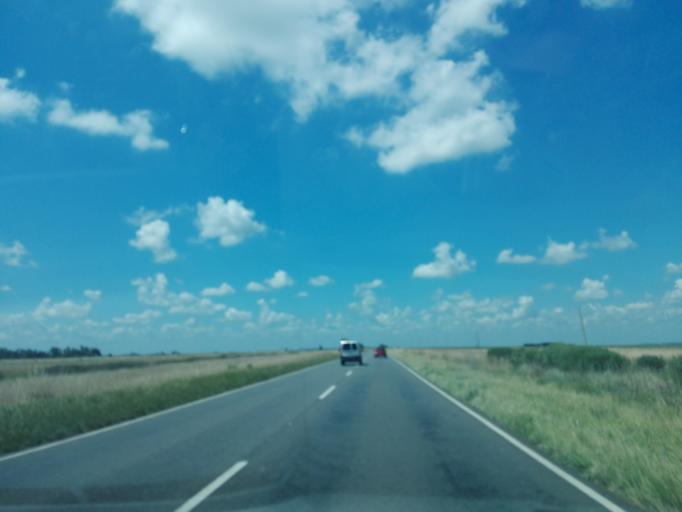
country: AR
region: Buenos Aires
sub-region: Partido de General Belgrano
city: General Belgrano
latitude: -35.9249
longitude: -58.6198
